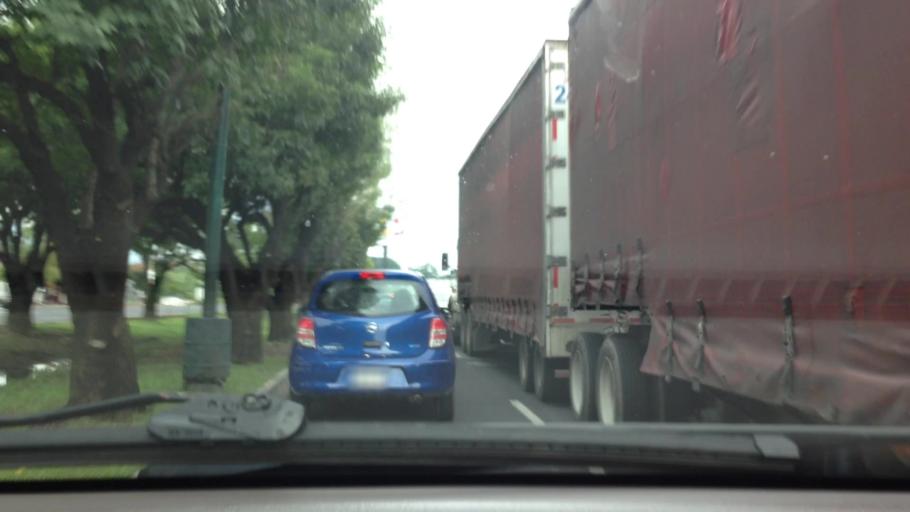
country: MX
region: Morelos
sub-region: Tepoztlan
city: Loma Bonita
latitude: 18.9188
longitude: -99.1901
